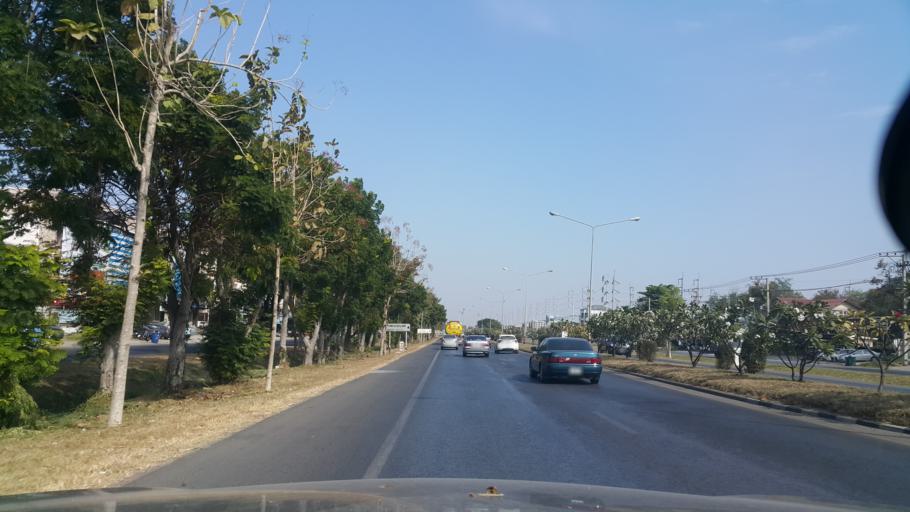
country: TH
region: Nakhon Ratchasima
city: Nakhon Ratchasima
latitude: 14.9505
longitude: 102.0537
